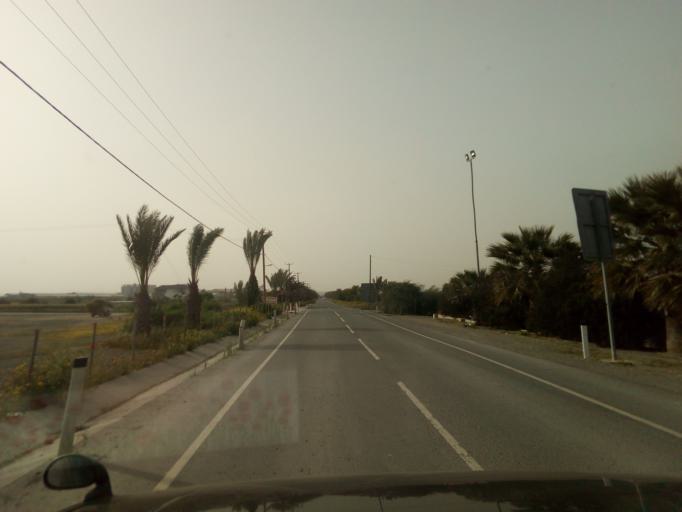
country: CY
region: Larnaka
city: Athienou
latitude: 35.0547
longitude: 33.5322
